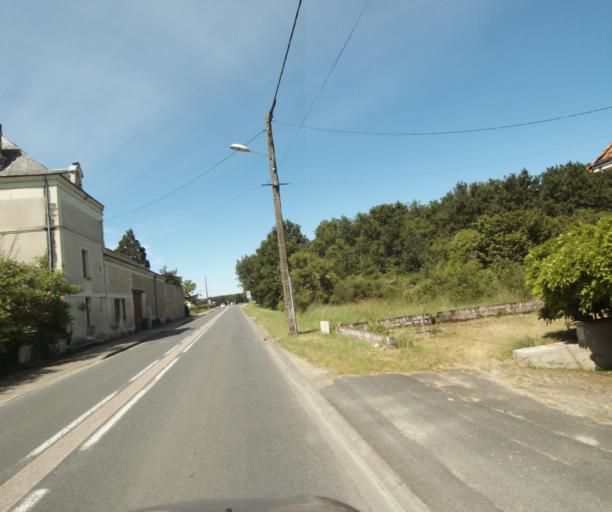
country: FR
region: Centre
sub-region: Departement d'Indre-et-Loire
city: Ligre
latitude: 47.1352
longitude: 0.3035
